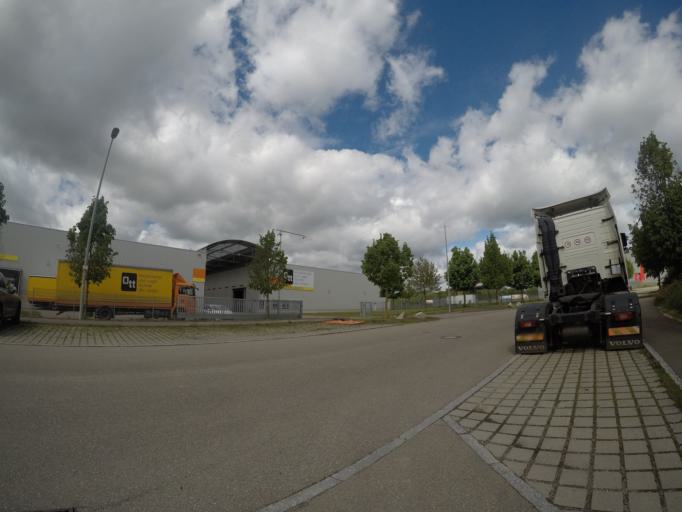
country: DE
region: Baden-Wuerttemberg
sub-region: Tuebingen Region
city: Dornstadt
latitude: 48.4537
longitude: 9.9680
